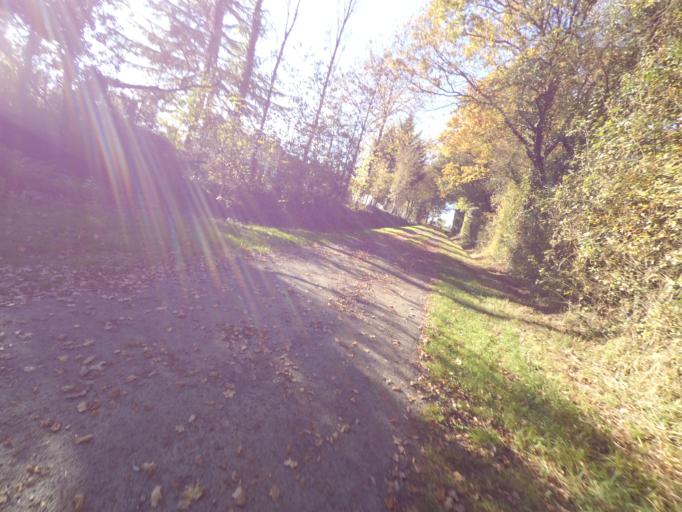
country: FR
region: Pays de la Loire
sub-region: Departement de la Vendee
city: Saint-Hilaire-de-Loulay
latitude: 46.9959
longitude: -1.3713
